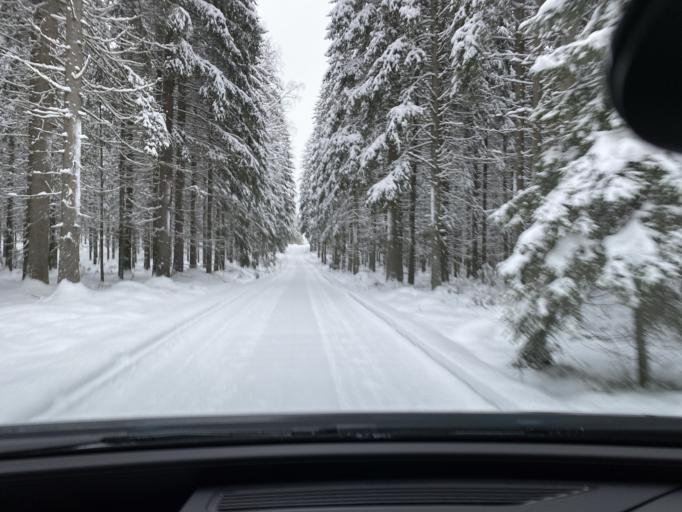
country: FI
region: Pirkanmaa
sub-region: Lounais-Pirkanmaa
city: Punkalaidun
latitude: 61.1318
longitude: 23.0939
